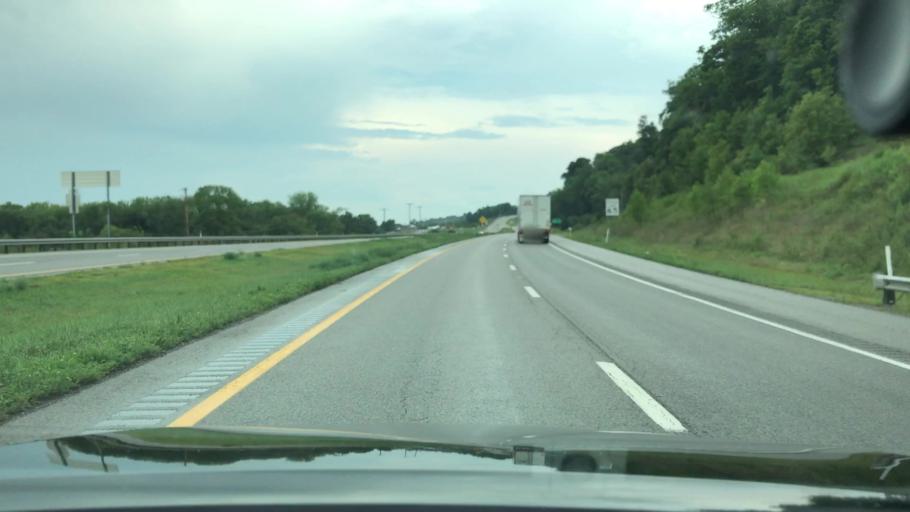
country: US
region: West Virginia
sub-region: Mason County
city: Point Pleasant
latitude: 38.8171
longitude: -82.1153
